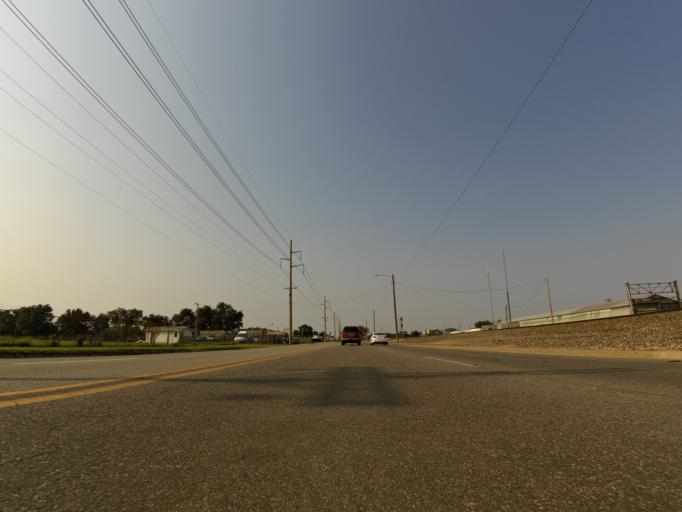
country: US
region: Kansas
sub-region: Sedgwick County
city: Park City
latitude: 37.7484
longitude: -97.3360
